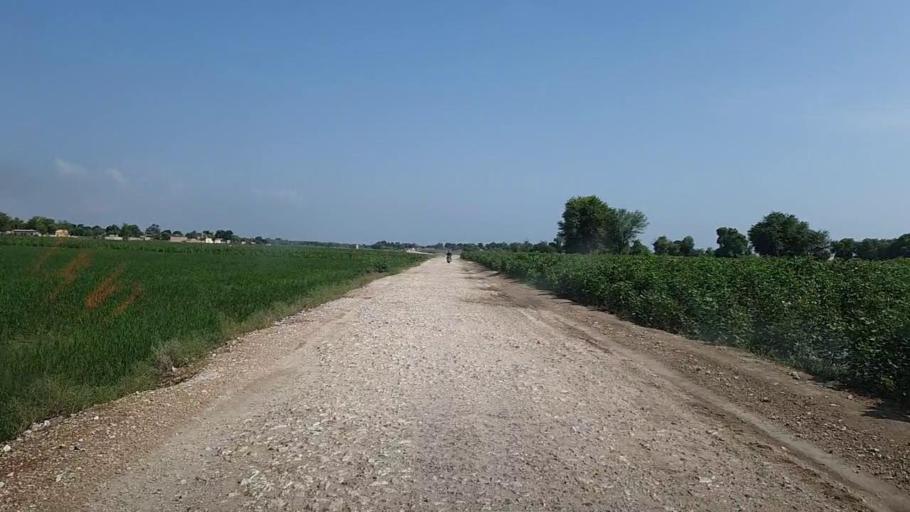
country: PK
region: Sindh
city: Bhiria
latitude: 26.8764
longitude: 68.2307
